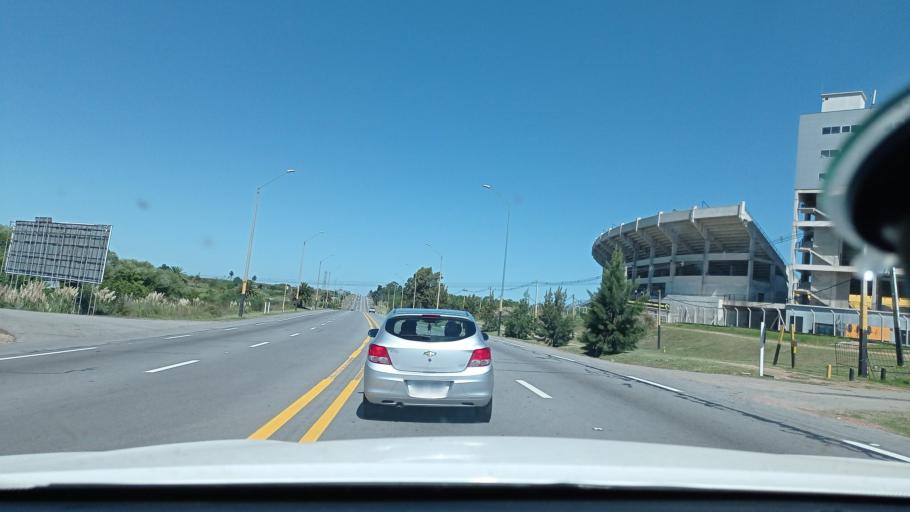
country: UY
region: Canelones
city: Colonia Nicolich
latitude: -34.7951
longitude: -56.0677
